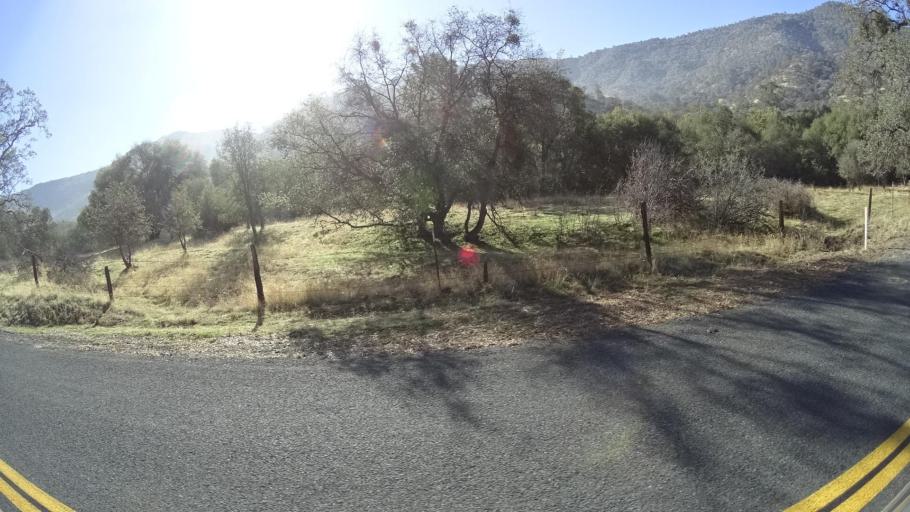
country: US
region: California
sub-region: Kern County
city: Alta Sierra
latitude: 35.7867
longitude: -118.7879
